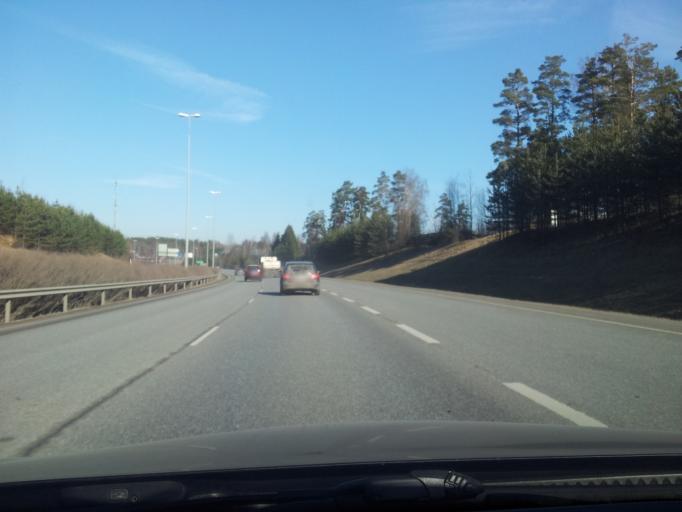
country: FI
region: Uusimaa
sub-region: Helsinki
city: Koukkuniemi
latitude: 60.1755
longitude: 24.7557
